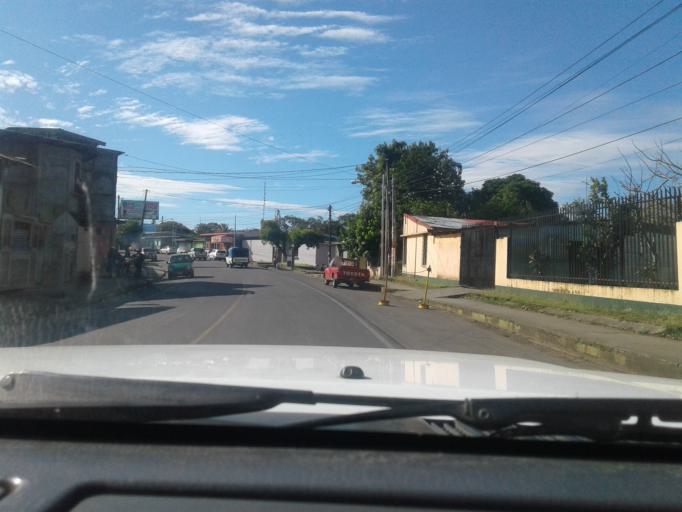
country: NI
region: Carazo
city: Jinotepe
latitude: 11.8525
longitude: -86.1977
